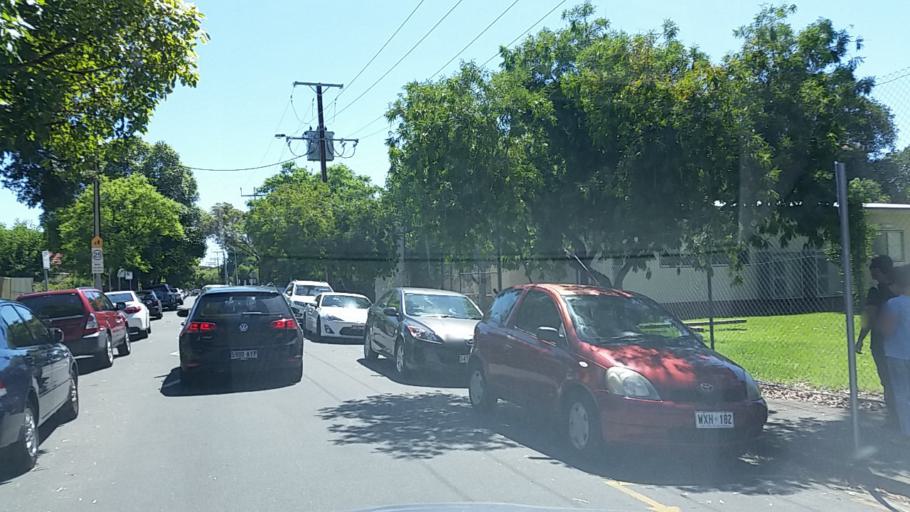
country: AU
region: South Australia
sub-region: Unley
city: Fullarton
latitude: -34.9449
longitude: 138.6210
